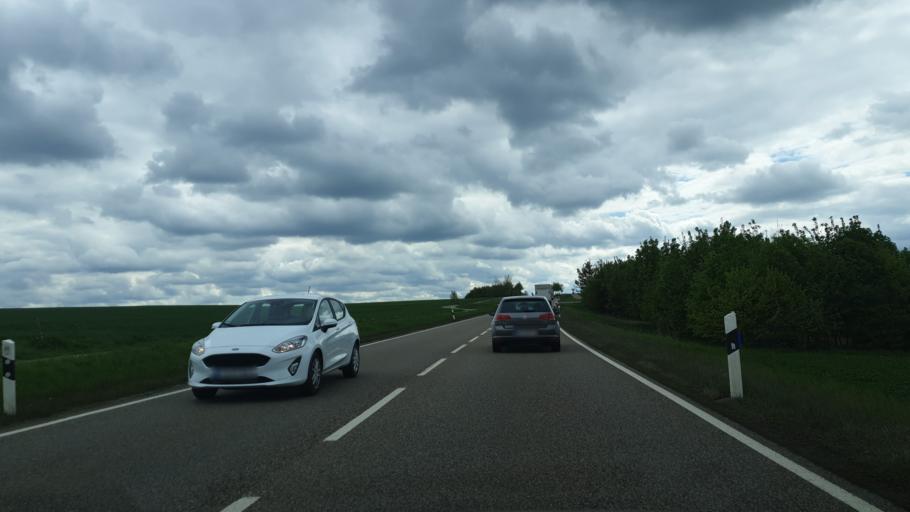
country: DE
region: Saxony
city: Hartenstein
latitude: 50.6754
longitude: 12.7011
